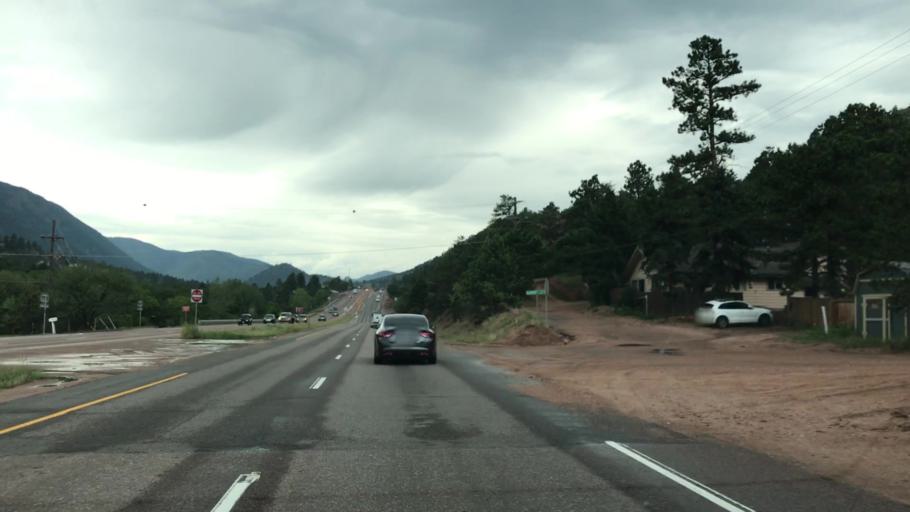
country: US
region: Colorado
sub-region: El Paso County
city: Cascade-Chipita Park
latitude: 38.9083
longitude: -104.9720
